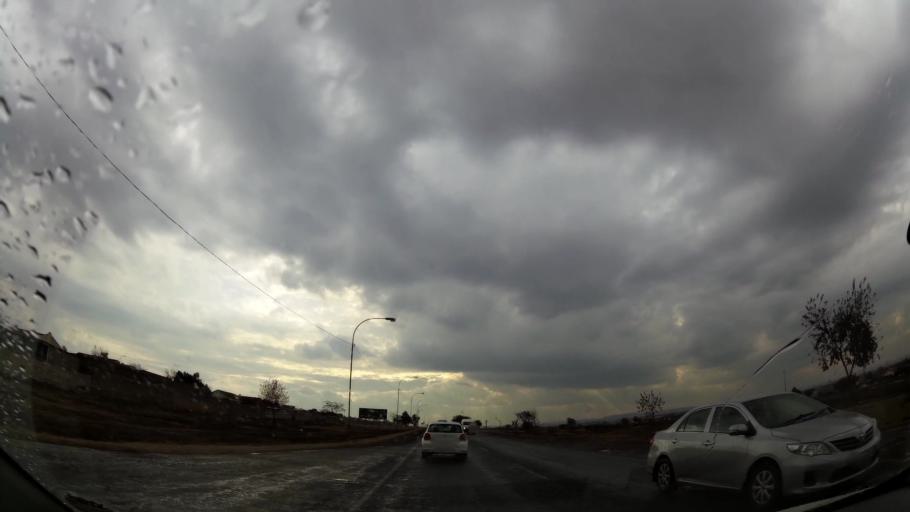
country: ZA
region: Gauteng
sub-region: Ekurhuleni Metropolitan Municipality
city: Germiston
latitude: -26.3738
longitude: 28.1315
